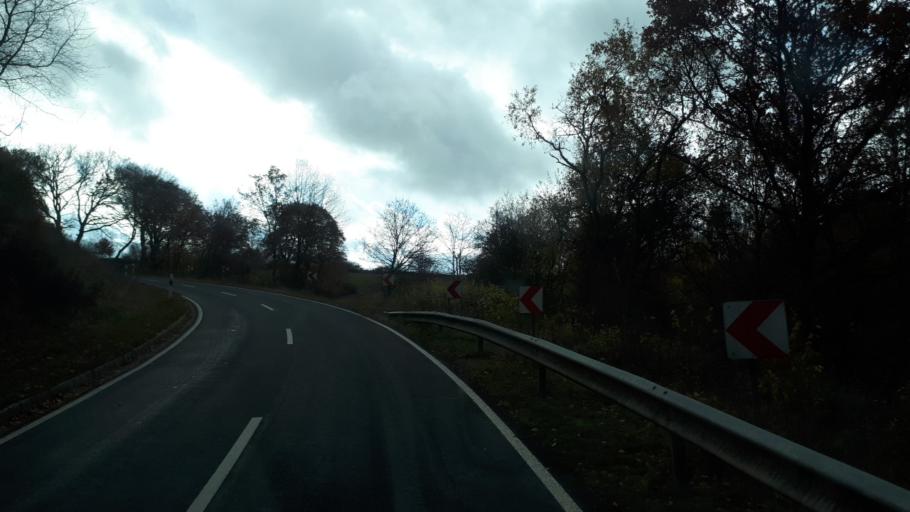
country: DE
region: Rheinland-Pfalz
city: Wirfus
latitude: 50.2079
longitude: 7.1984
